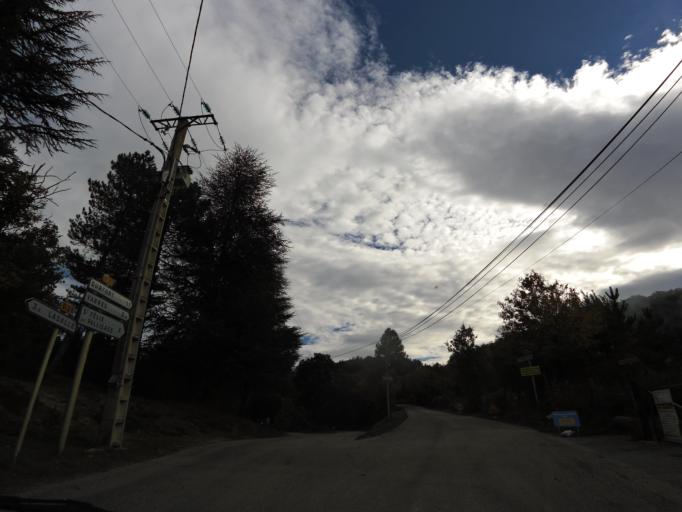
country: FR
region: Languedoc-Roussillon
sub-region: Departement du Gard
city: Lasalle
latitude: 44.0305
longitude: 3.8762
